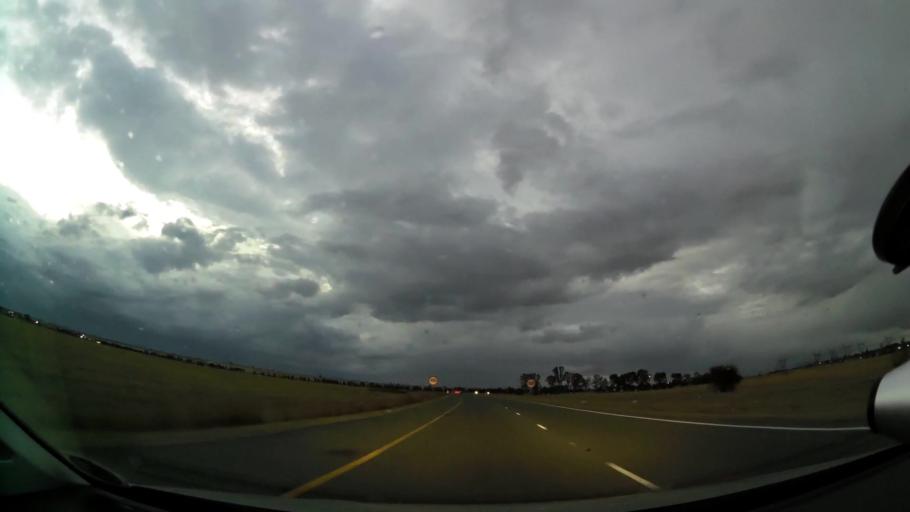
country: ZA
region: Orange Free State
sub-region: Lejweleputswa District Municipality
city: Welkom
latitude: -27.9480
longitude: 26.7958
